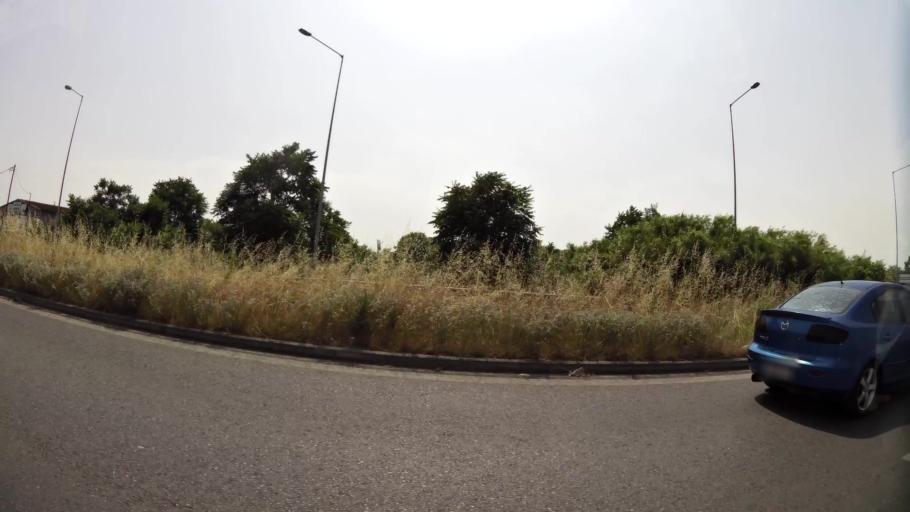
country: GR
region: Central Macedonia
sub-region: Nomos Thessalonikis
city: Nea Magnisia
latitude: 40.6916
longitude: 22.8476
